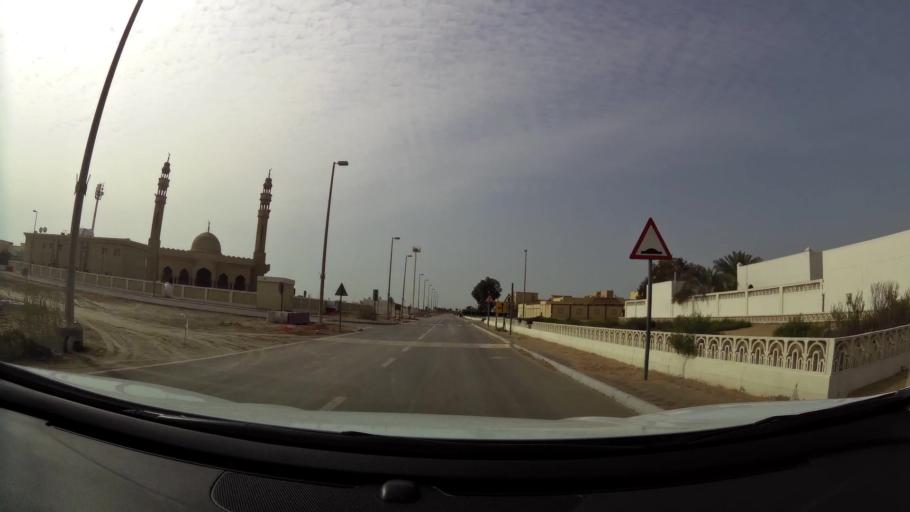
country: AE
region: Abu Dhabi
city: Abu Dhabi
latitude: 24.5921
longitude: 54.6960
